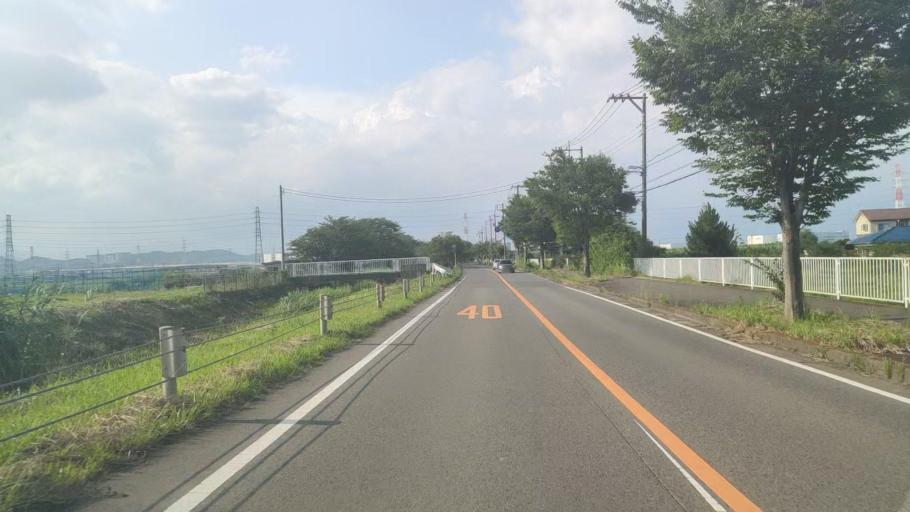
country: JP
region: Kanagawa
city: Isehara
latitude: 35.3918
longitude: 139.3379
